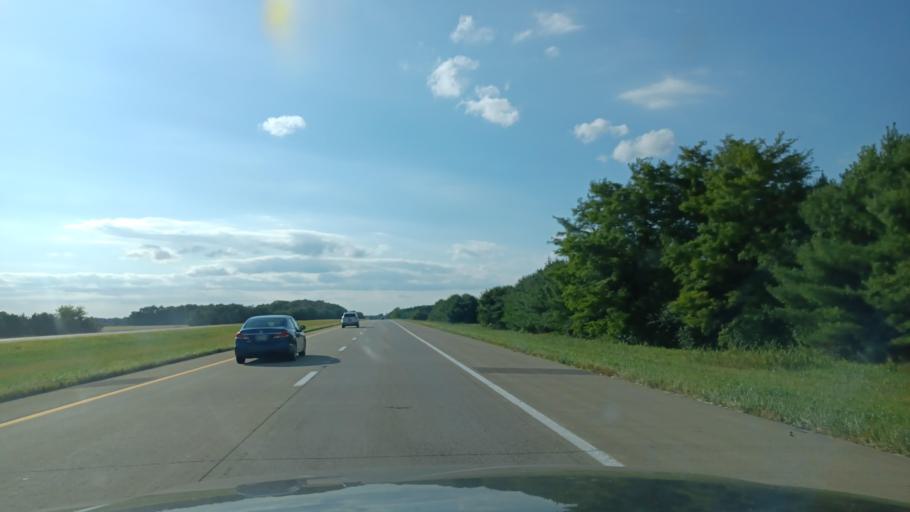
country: US
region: Ohio
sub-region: Greene County
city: Wilberforce
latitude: 39.6874
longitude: -83.8561
